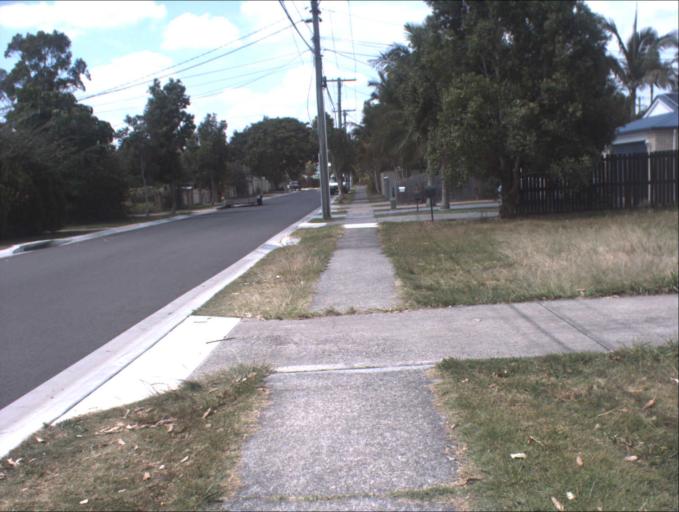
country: AU
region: Queensland
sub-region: Logan
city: Slacks Creek
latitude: -27.6455
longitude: 153.1584
